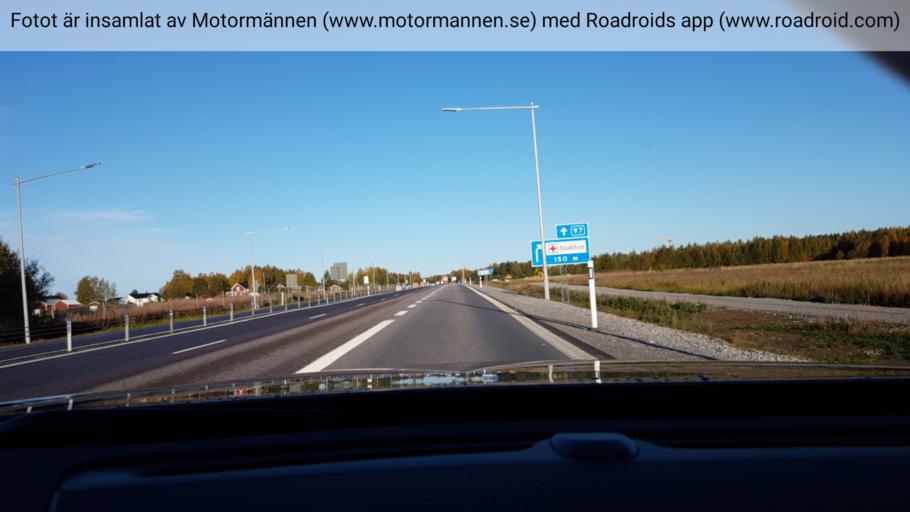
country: SE
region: Norrbotten
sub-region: Lulea Kommun
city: Sodra Sunderbyn
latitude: 65.6640
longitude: 21.9510
